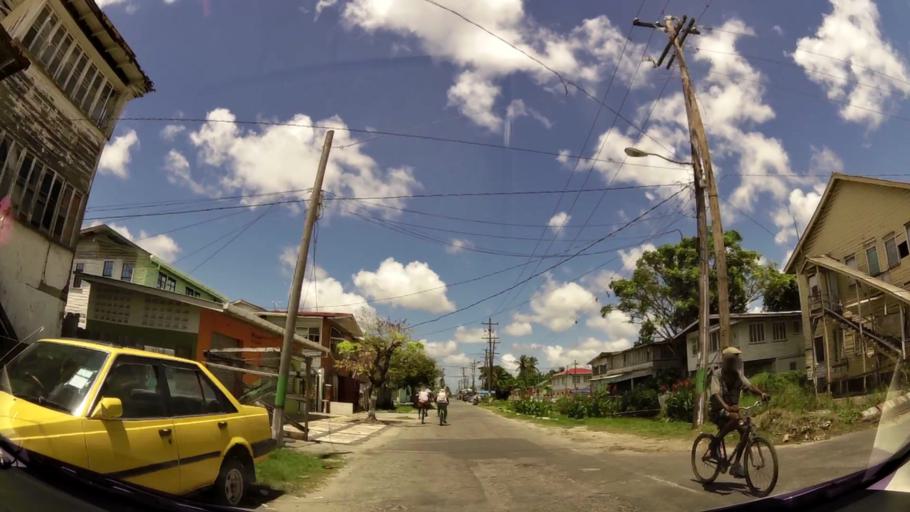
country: GY
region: Demerara-Mahaica
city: Georgetown
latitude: 6.8005
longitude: -58.1647
